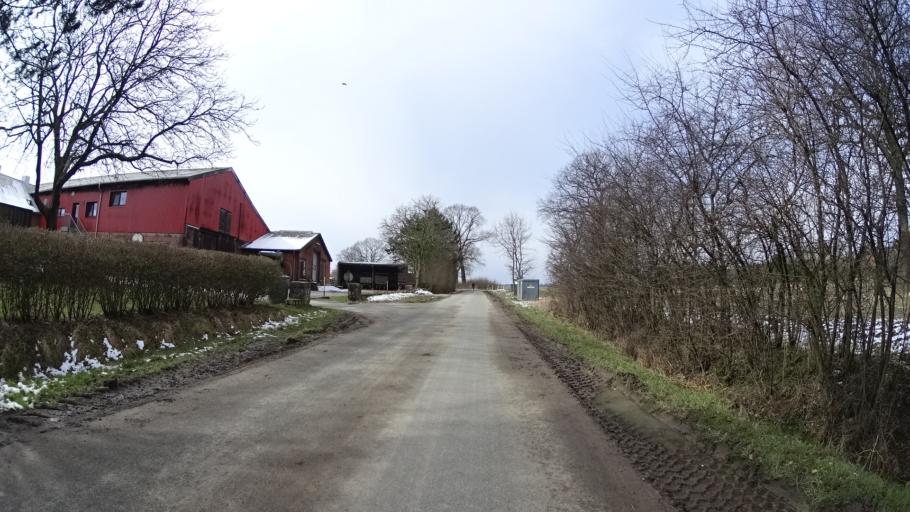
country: DE
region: Schleswig-Holstein
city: Rendswuhren
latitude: 54.0961
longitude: 10.1877
